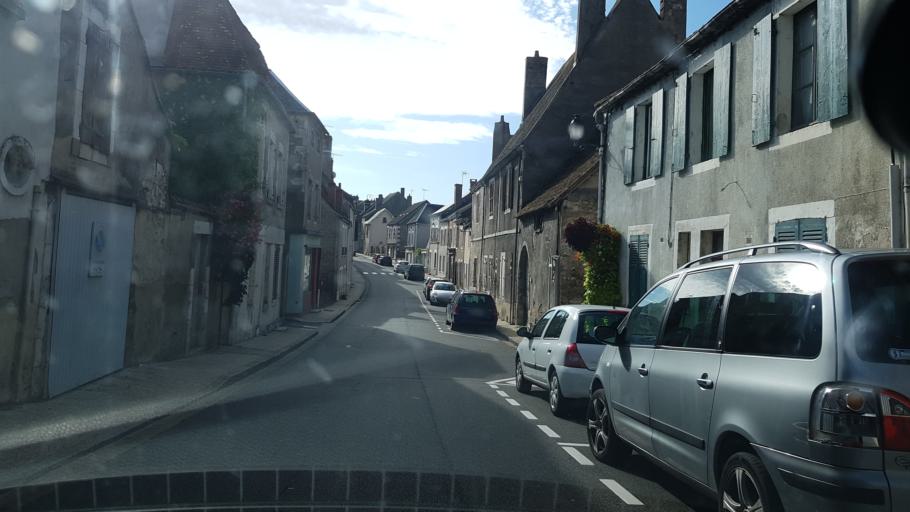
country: FR
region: Centre
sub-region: Departement du Loiret
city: Bonny-sur-Loire
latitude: 47.5619
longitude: 2.8378
